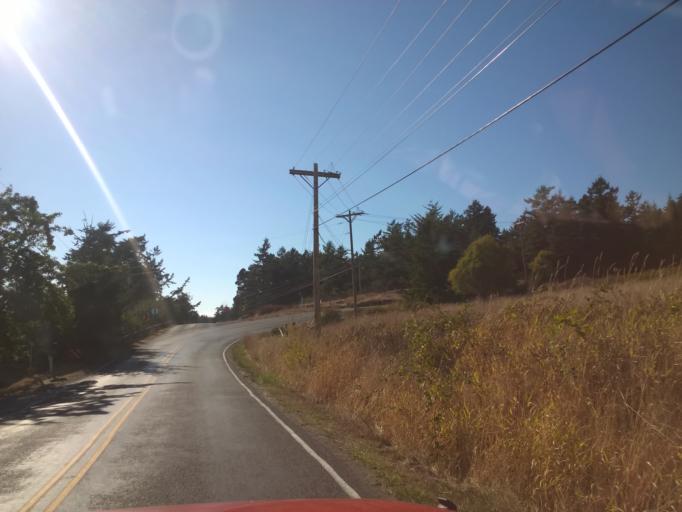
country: US
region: Washington
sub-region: San Juan County
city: Friday Harbor
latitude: 48.4710
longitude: -122.8982
